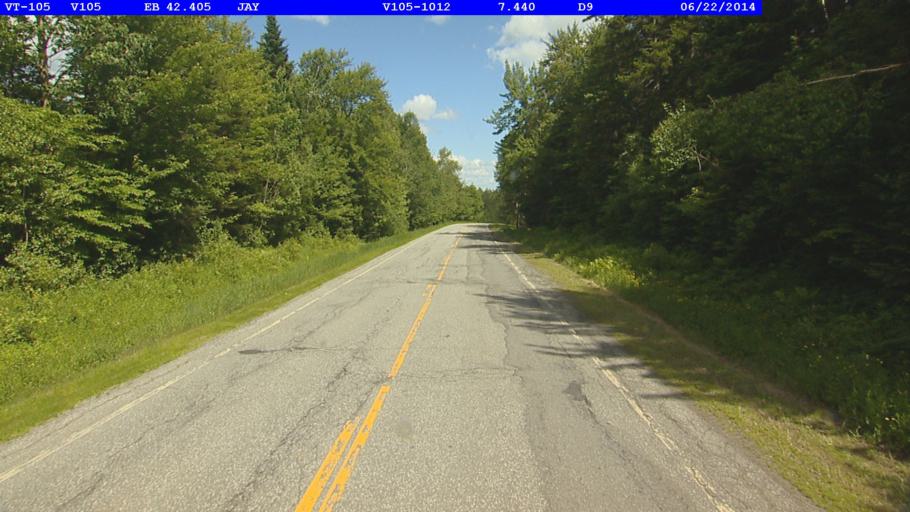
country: CA
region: Quebec
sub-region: Monteregie
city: Sutton
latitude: 44.9677
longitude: -72.4401
